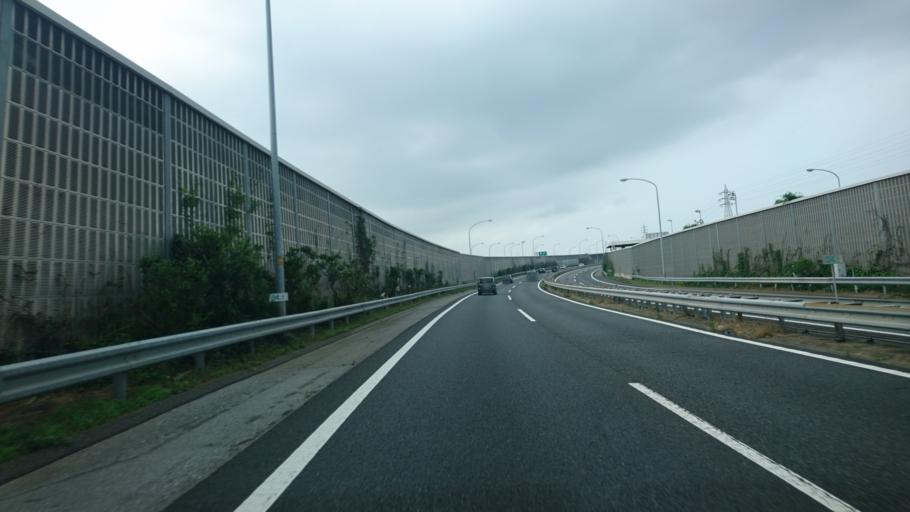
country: JP
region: Chiba
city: Chiba
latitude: 35.5684
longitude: 140.1377
